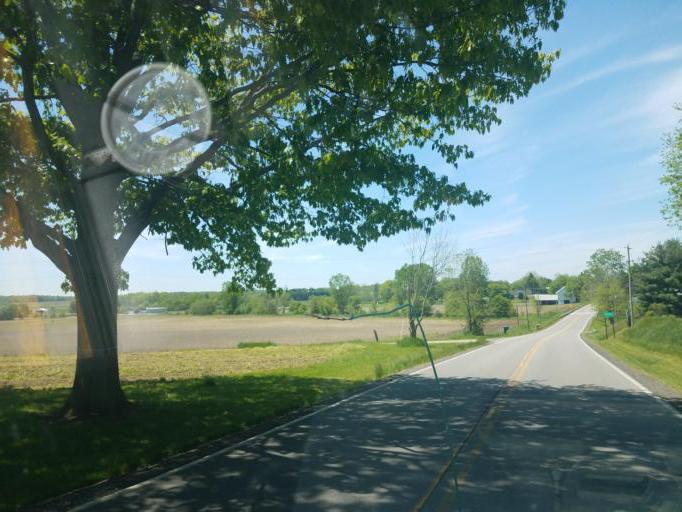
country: US
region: Ohio
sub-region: Ashland County
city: Ashland
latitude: 40.9608
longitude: -82.3592
